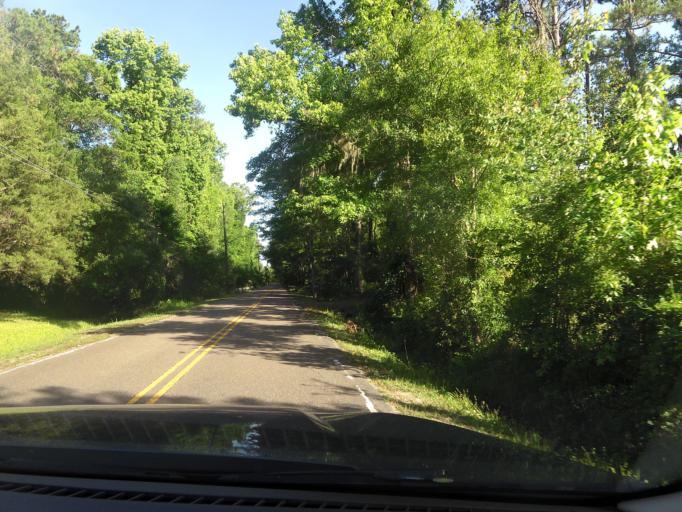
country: US
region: Florida
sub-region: Nassau County
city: Nassau Village-Ratliff
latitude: 30.4624
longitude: -81.8332
